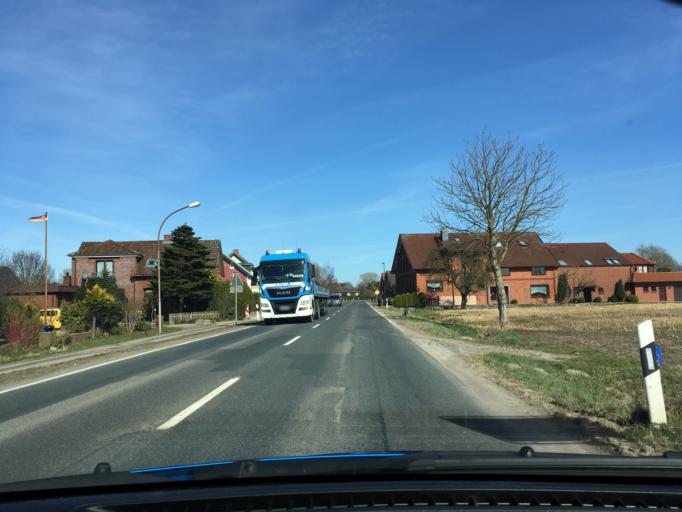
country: DE
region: Lower Saxony
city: Drage
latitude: 53.4201
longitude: 10.2823
